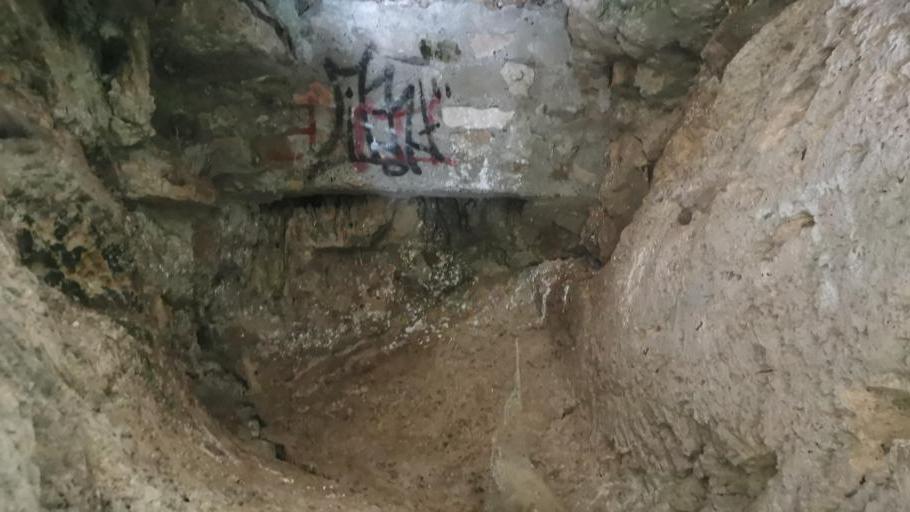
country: FR
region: Provence-Alpes-Cote d'Azur
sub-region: Departement du Vaucluse
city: Beaumont-de-Pertuis
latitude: 43.6875
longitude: 5.7072
